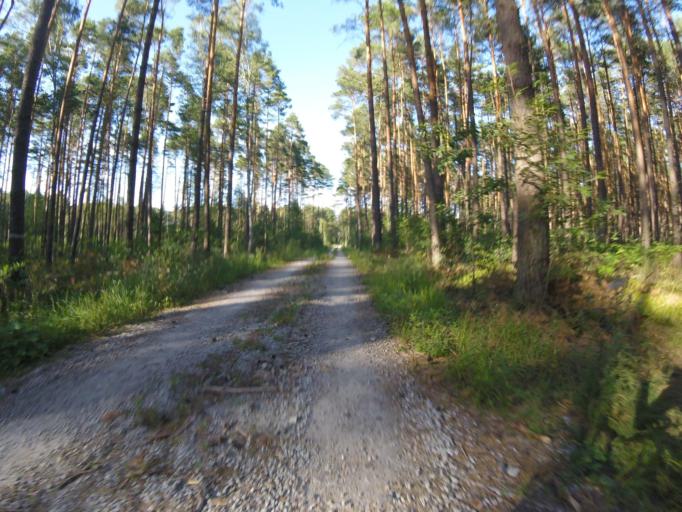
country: DE
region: Brandenburg
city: Erkner
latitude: 52.3347
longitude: 13.7408
